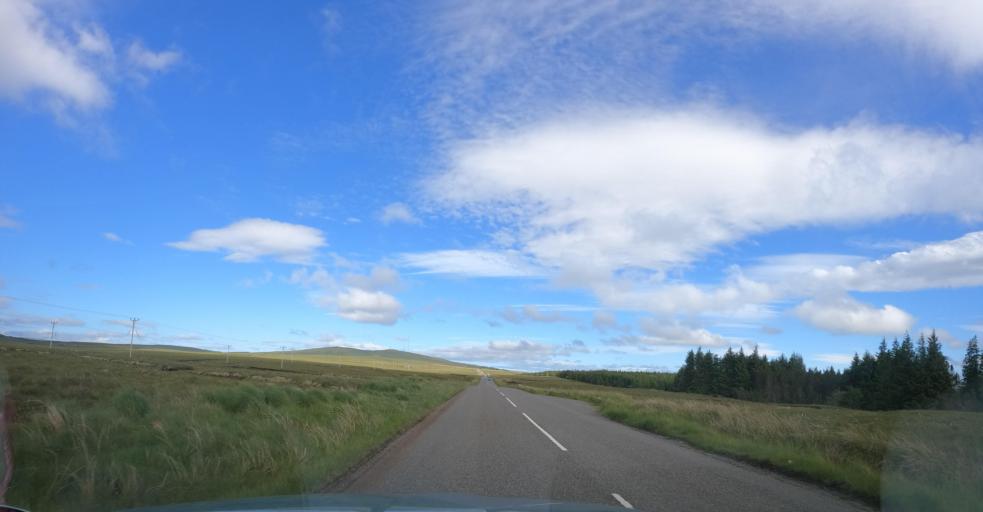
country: GB
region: Scotland
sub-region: Eilean Siar
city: Isle of Lewis
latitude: 58.1803
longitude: -6.6548
